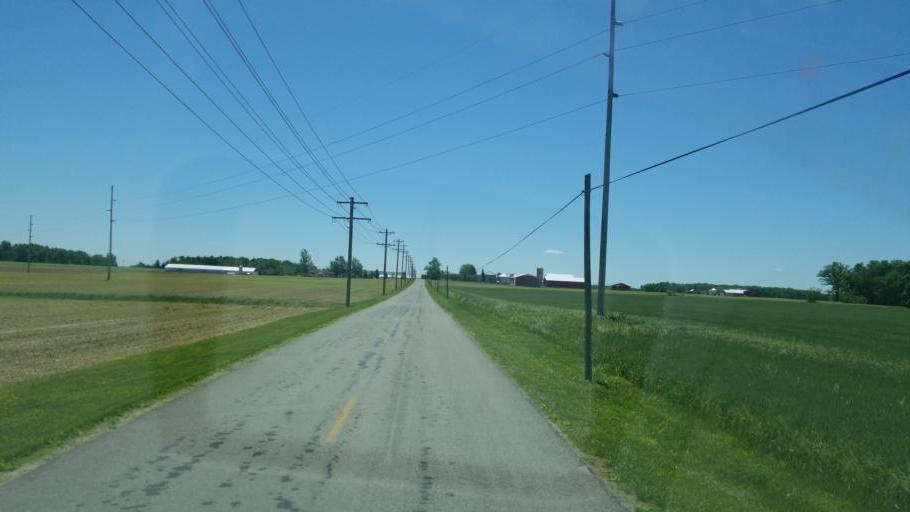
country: US
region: Ohio
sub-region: Mercer County
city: Fort Recovery
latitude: 40.3763
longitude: -84.7290
